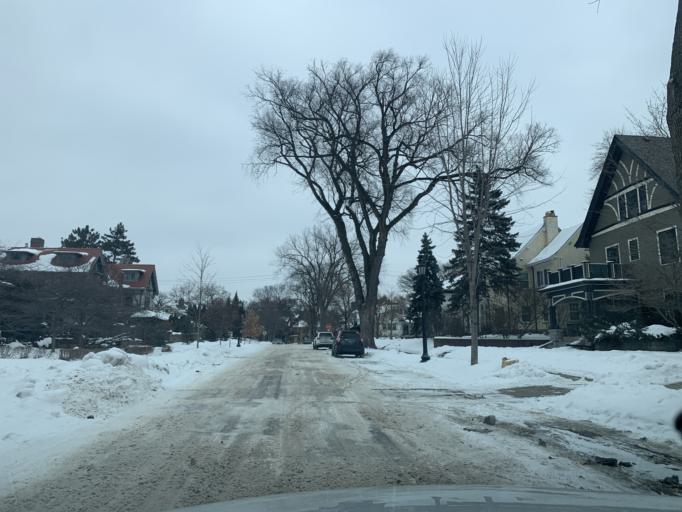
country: US
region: Minnesota
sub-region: Hennepin County
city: Minneapolis
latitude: 44.9646
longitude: -93.2969
